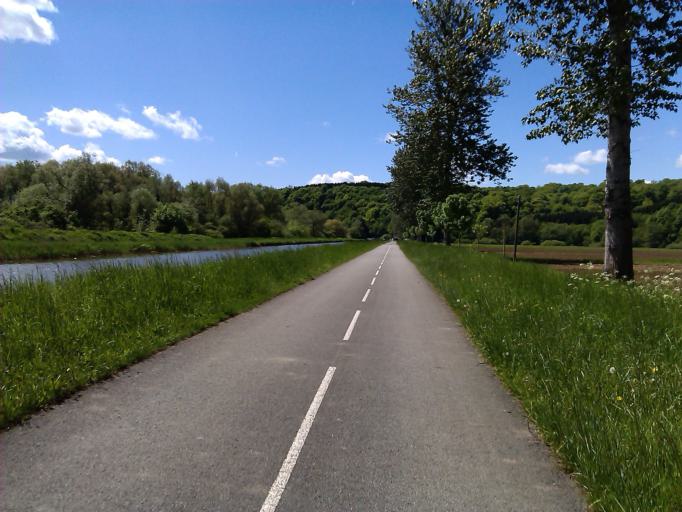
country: FR
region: Franche-Comte
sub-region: Territoire de Belfort
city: Bourogne
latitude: 47.5511
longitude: 6.9133
